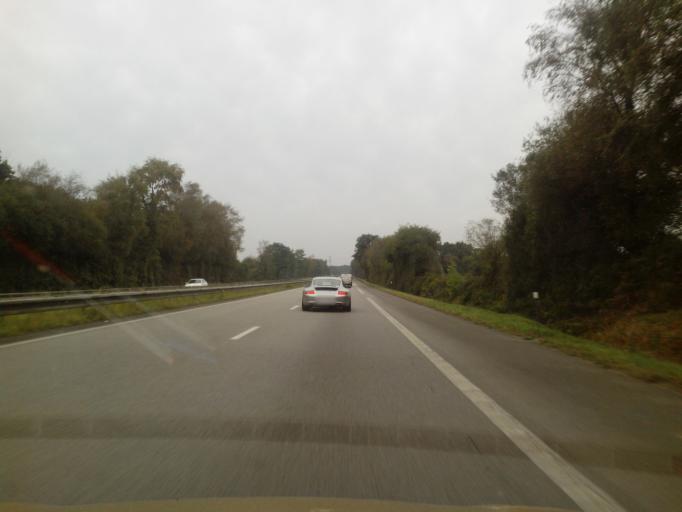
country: FR
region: Brittany
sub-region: Departement du Morbihan
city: Languidic
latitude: 47.8546
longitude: -3.1174
